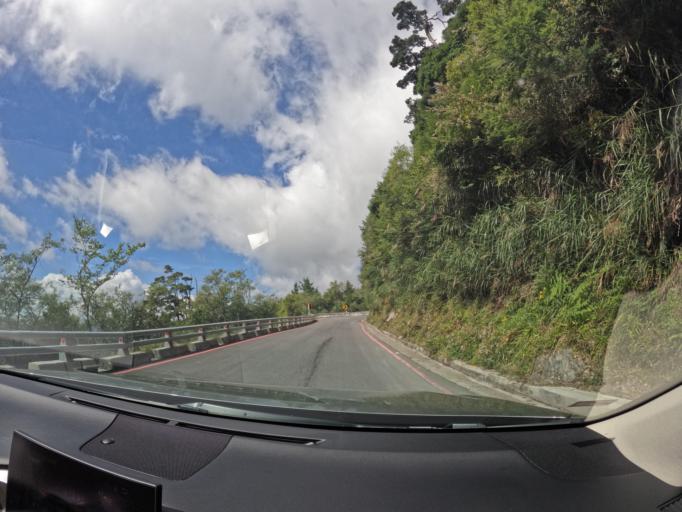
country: TW
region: Taiwan
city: Yujing
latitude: 23.2630
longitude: 120.9487
